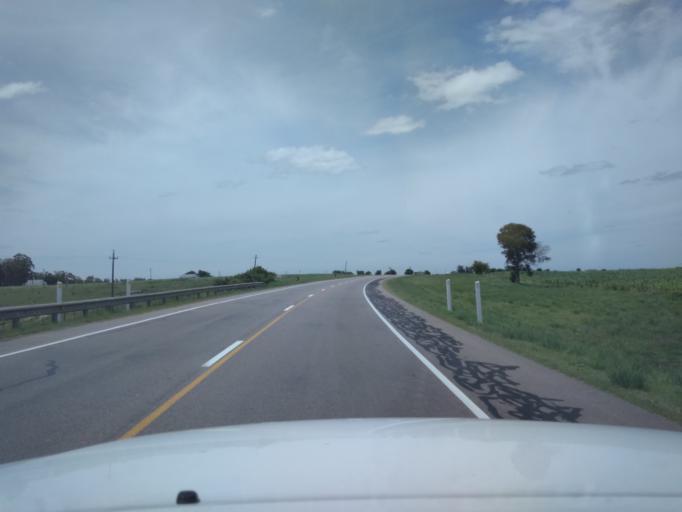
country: UY
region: Florida
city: Cardal
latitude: -34.3183
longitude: -56.2424
